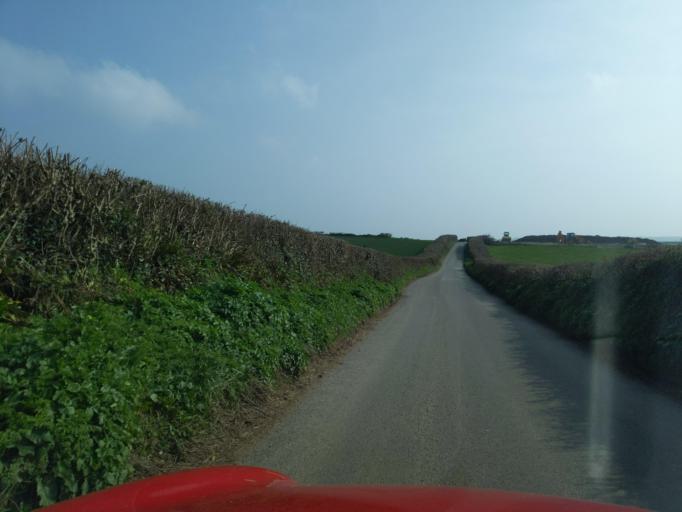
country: GB
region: England
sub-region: Devon
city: Salcombe
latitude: 50.2636
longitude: -3.7183
